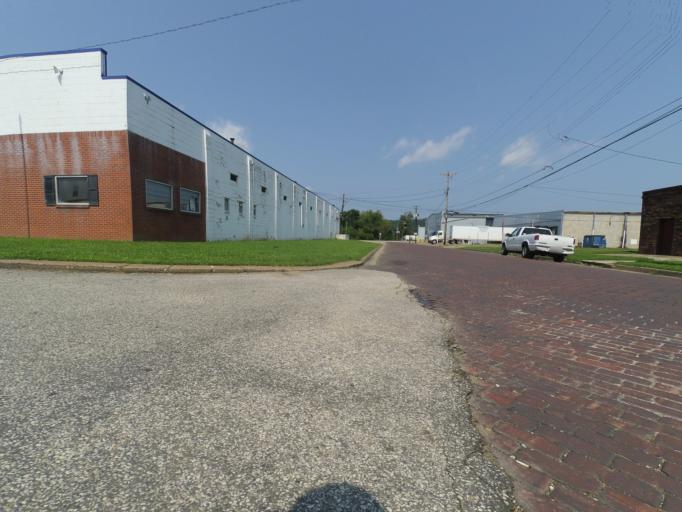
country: US
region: West Virginia
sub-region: Cabell County
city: Huntington
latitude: 38.4315
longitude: -82.4107
